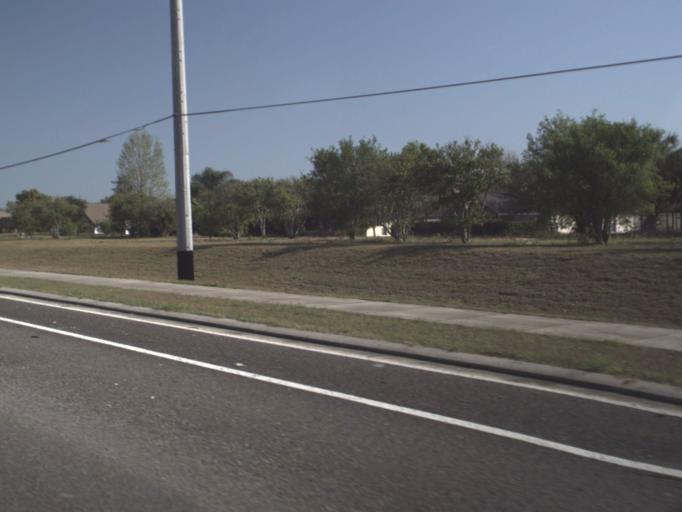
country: US
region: Florida
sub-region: Lake County
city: Four Corners
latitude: 28.3917
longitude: -81.6925
